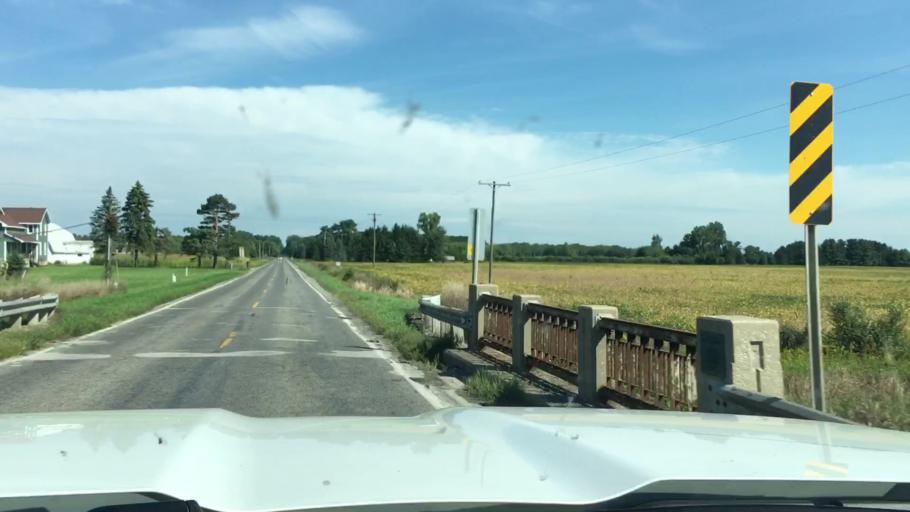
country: US
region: Michigan
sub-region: Saginaw County
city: Hemlock
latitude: 43.4512
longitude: -84.2302
